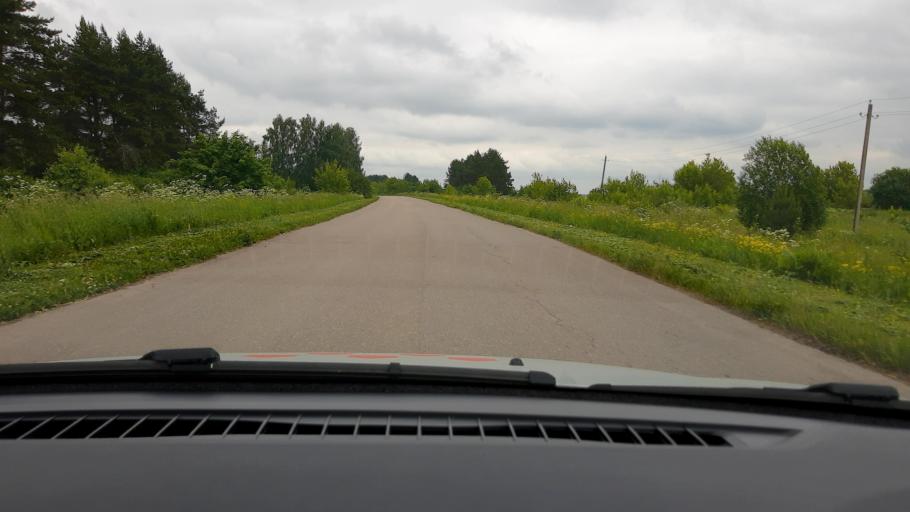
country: RU
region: Nizjnij Novgorod
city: Bogorodsk
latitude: 56.0637
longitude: 43.4995
